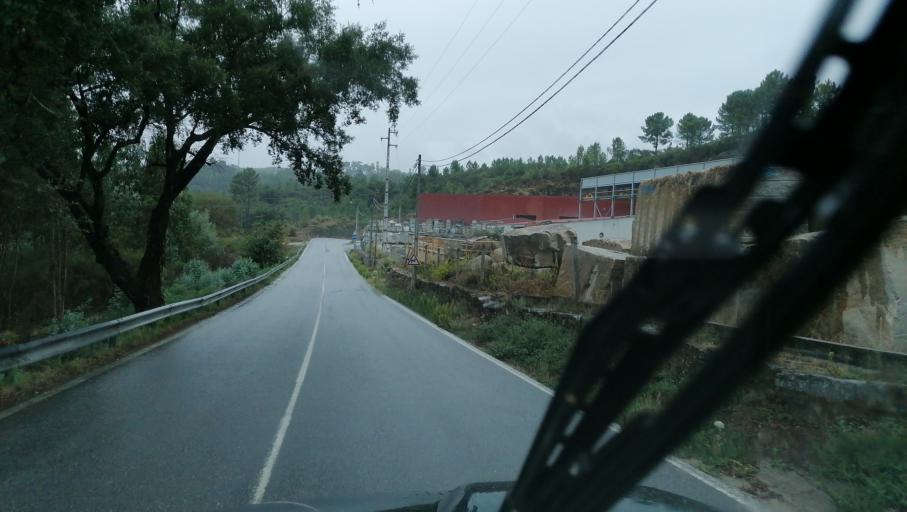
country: PT
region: Braga
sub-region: Cabeceiras de Basto
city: Cabeceiras de Basto
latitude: 41.4933
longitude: -7.9401
